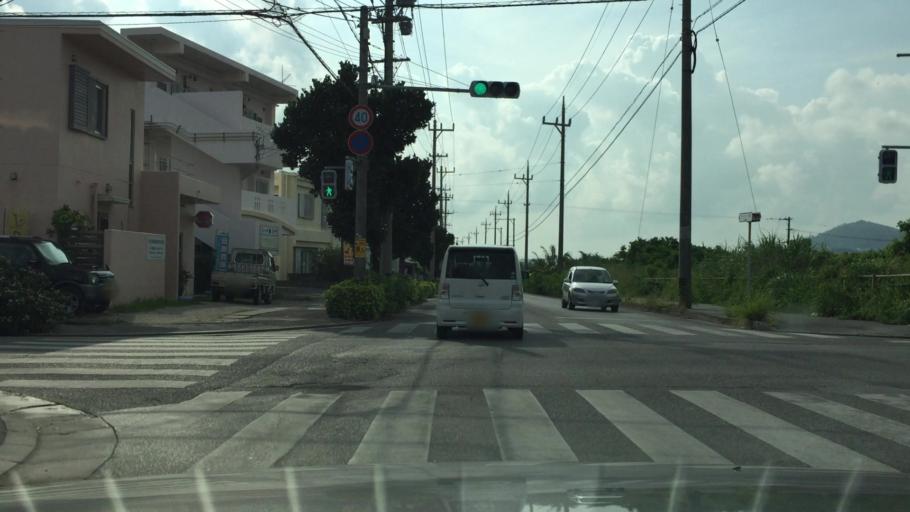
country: JP
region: Okinawa
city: Ishigaki
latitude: 24.3493
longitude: 124.1642
